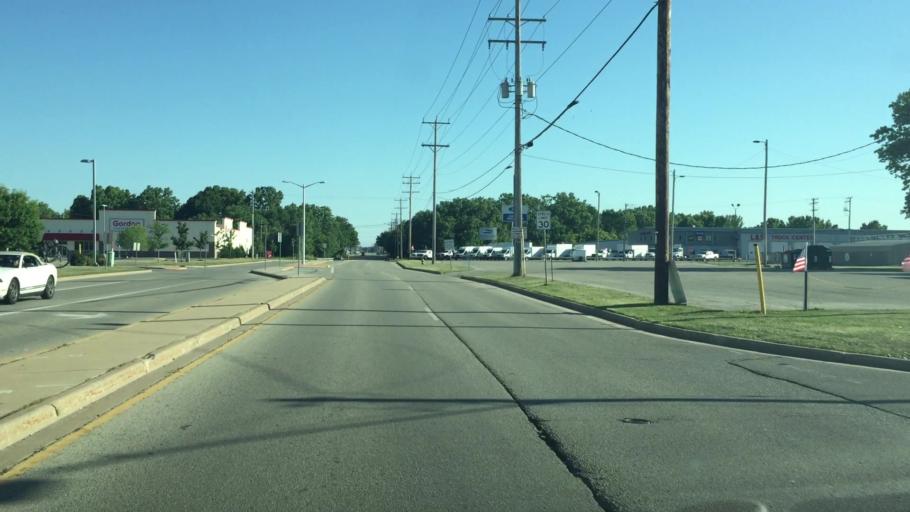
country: US
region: Wisconsin
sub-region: Outagamie County
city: Appleton
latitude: 44.2621
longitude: -88.4558
